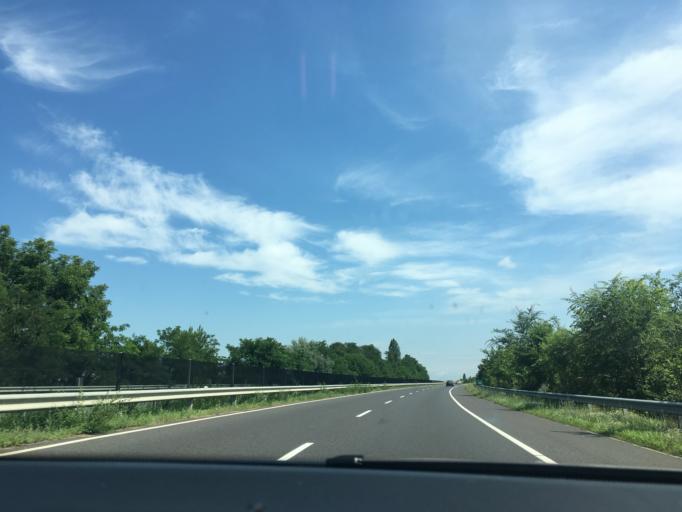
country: HU
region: Szabolcs-Szatmar-Bereg
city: Nyiregyhaza
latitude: 47.8941
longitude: 21.7097
